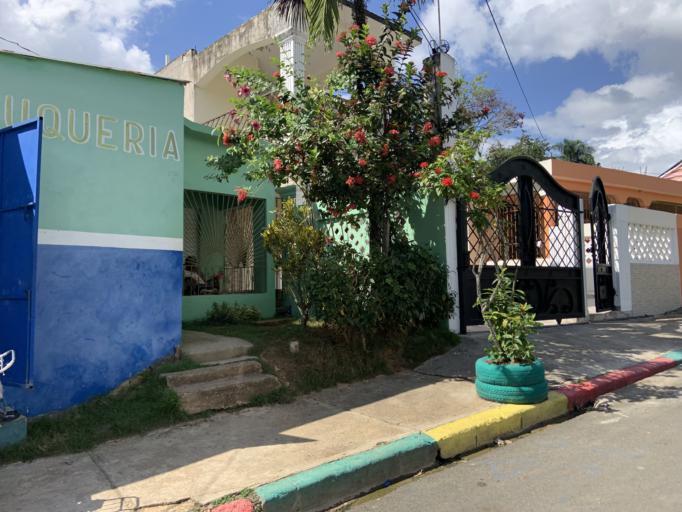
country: DO
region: Monte Plata
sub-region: Yamasa
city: Yamasa
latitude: 18.7693
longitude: -70.0258
